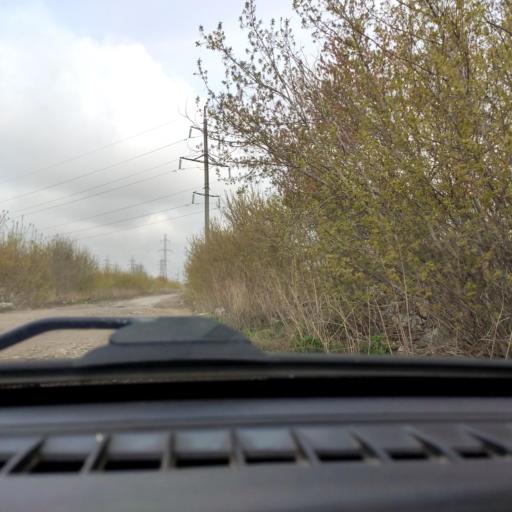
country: RU
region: Samara
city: Zhigulevsk
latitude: 53.5372
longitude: 49.5021
